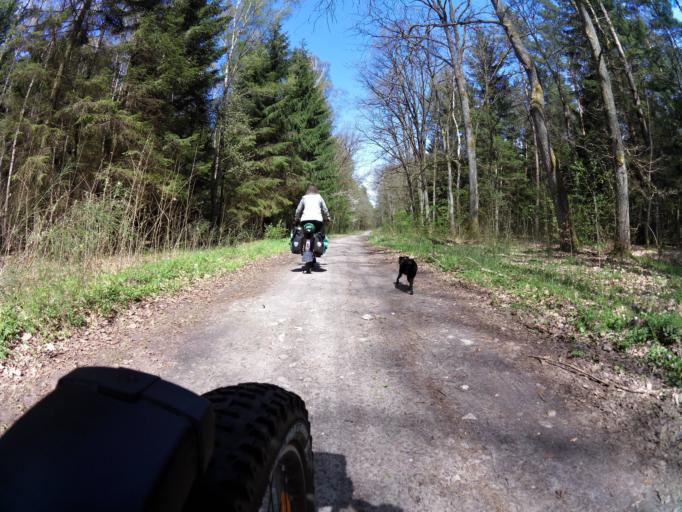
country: PL
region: West Pomeranian Voivodeship
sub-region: Powiat lobeski
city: Resko
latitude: 53.8074
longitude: 15.4464
